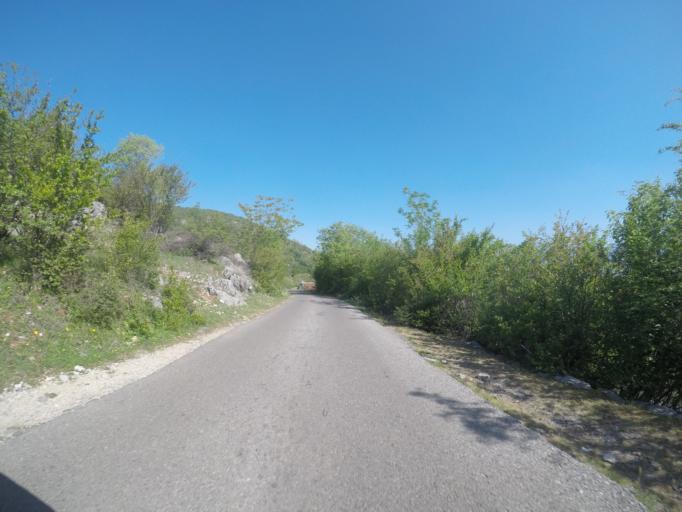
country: ME
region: Danilovgrad
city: Danilovgrad
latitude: 42.5325
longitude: 19.0901
